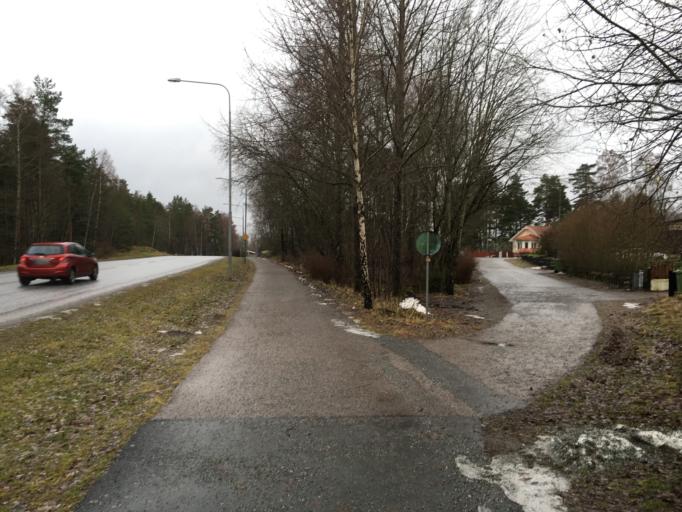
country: SE
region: Uppsala
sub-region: Knivsta Kommun
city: Knivsta
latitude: 59.7339
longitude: 17.7959
